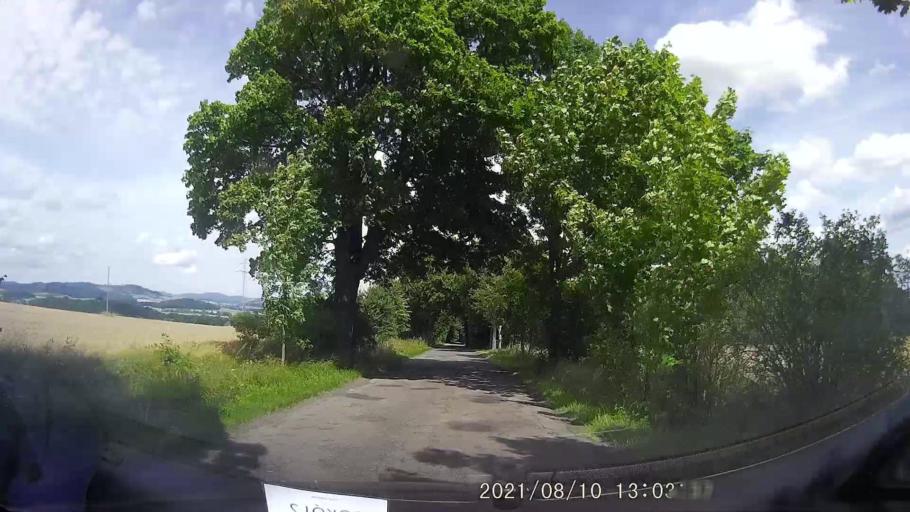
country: PL
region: Lower Silesian Voivodeship
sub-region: Powiat klodzki
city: Bozkow
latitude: 50.4720
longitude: 16.5626
